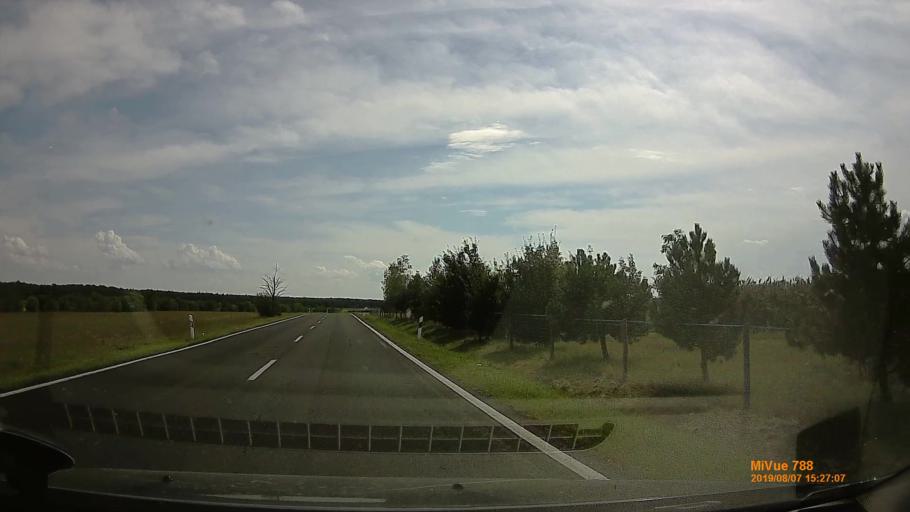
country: HU
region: Vas
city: Buk
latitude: 47.2973
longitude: 16.8212
